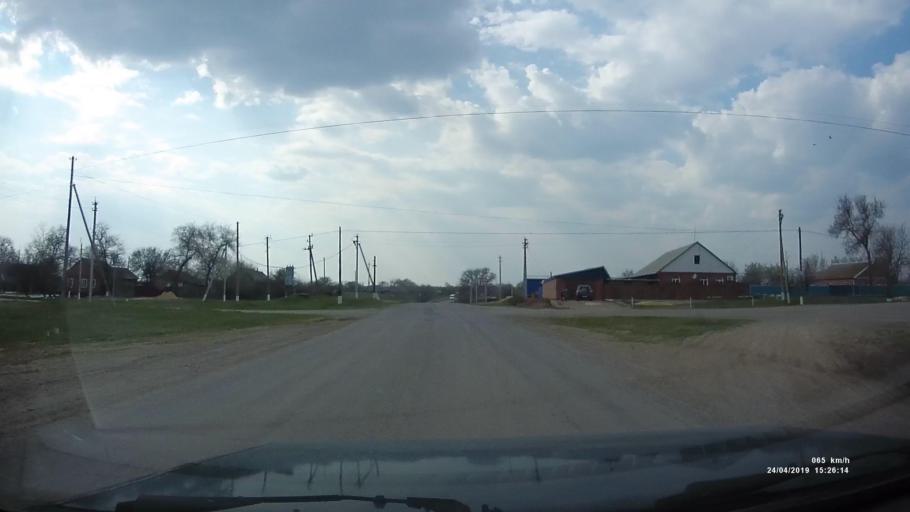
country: RU
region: Rostov
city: Remontnoye
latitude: 46.5574
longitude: 43.0352
